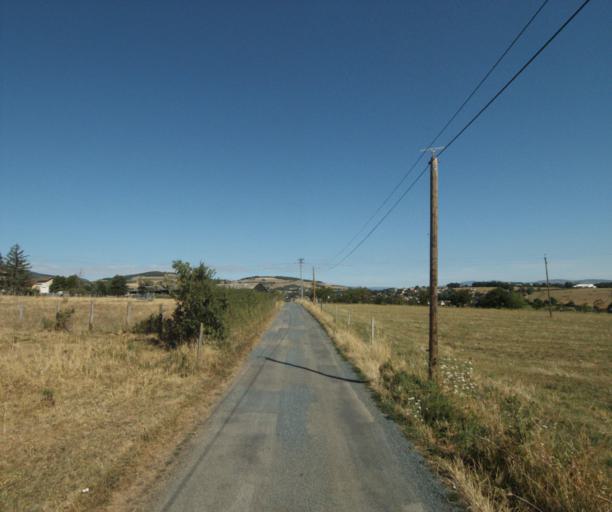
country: FR
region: Rhone-Alpes
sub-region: Departement du Rhone
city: Sain-Bel
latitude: 45.8069
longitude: 4.5866
